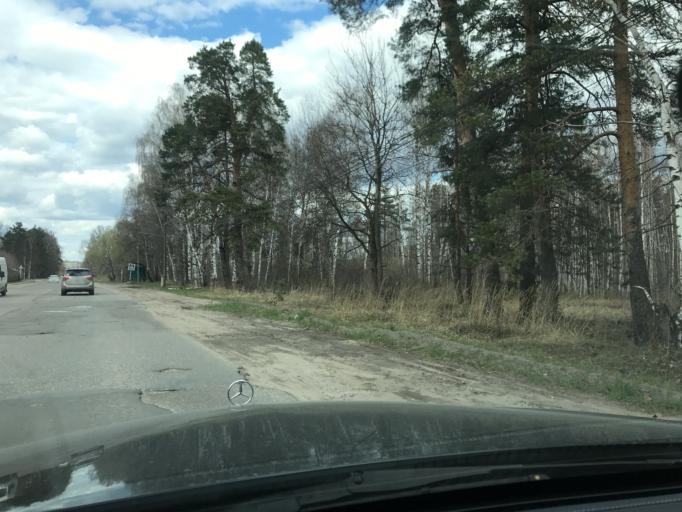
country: RU
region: Vladimir
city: Pokrov
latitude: 55.9039
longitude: 39.1910
